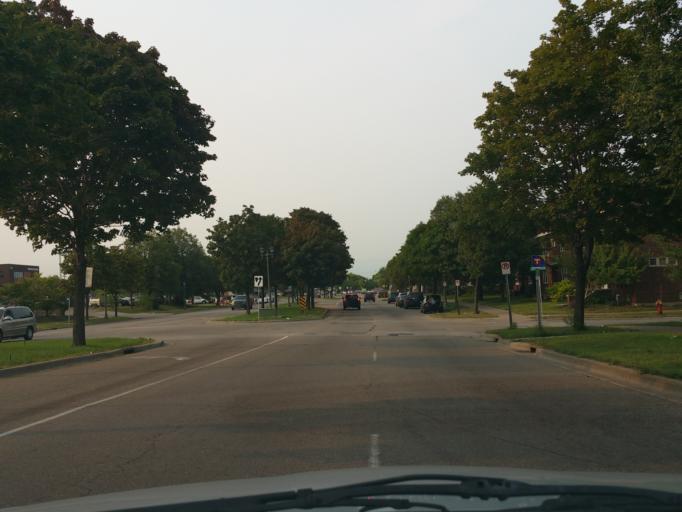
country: US
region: Minnesota
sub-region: Ramsey County
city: Falcon Heights
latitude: 44.9527
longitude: -93.1465
